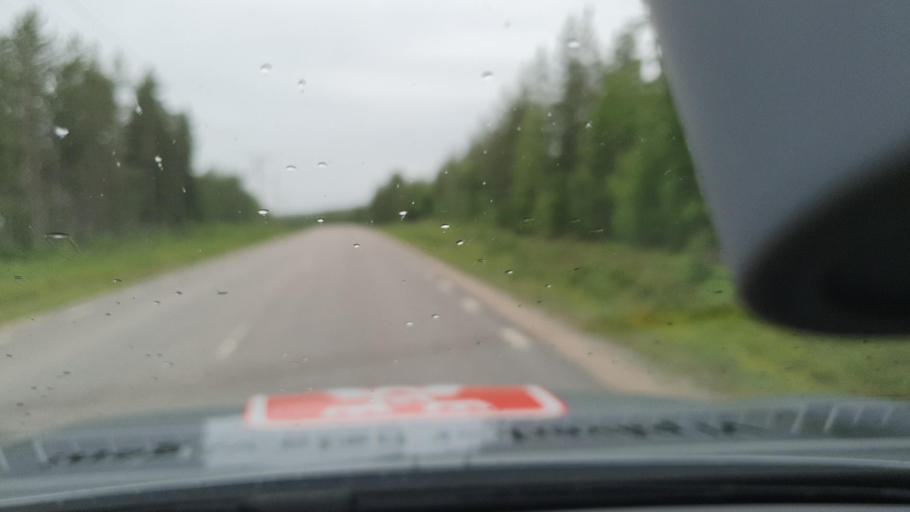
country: SE
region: Norrbotten
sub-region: Overtornea Kommun
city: OEvertornea
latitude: 66.3977
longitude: 23.5798
